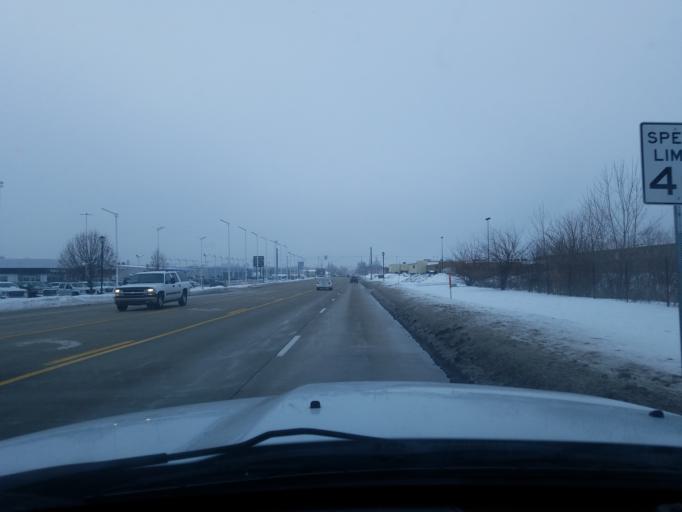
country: US
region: Indiana
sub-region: Saint Joseph County
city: Georgetown
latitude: 41.7095
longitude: -86.1845
